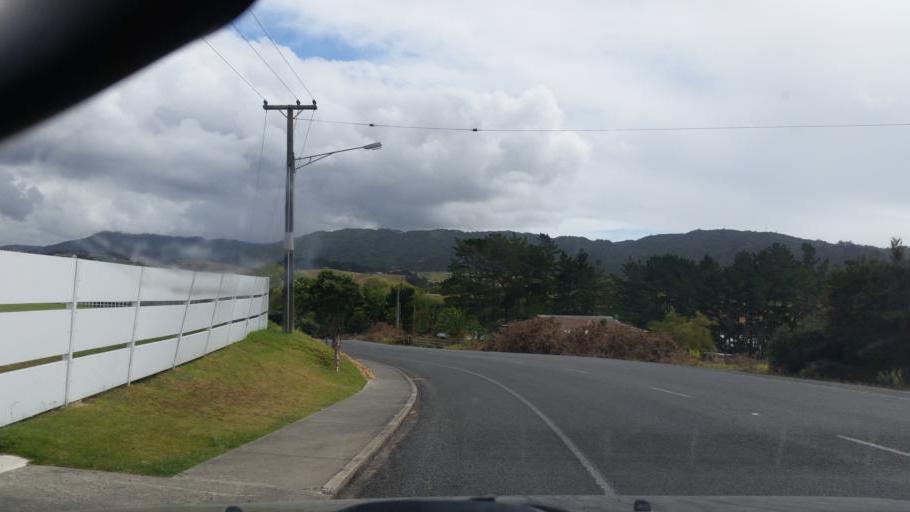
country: NZ
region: Auckland
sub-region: Auckland
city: Wellsford
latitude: -36.0861
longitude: 174.5793
